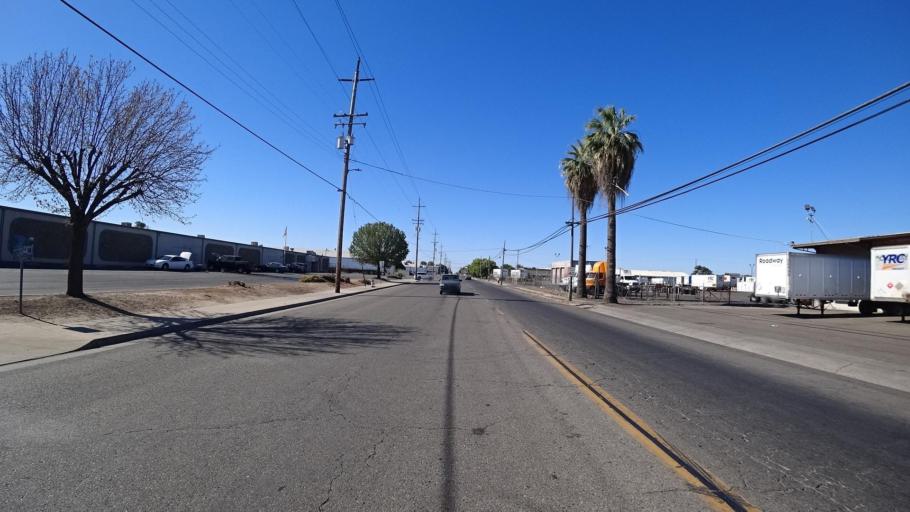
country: US
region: California
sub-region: Fresno County
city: Fresno
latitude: 36.7136
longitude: -119.7817
